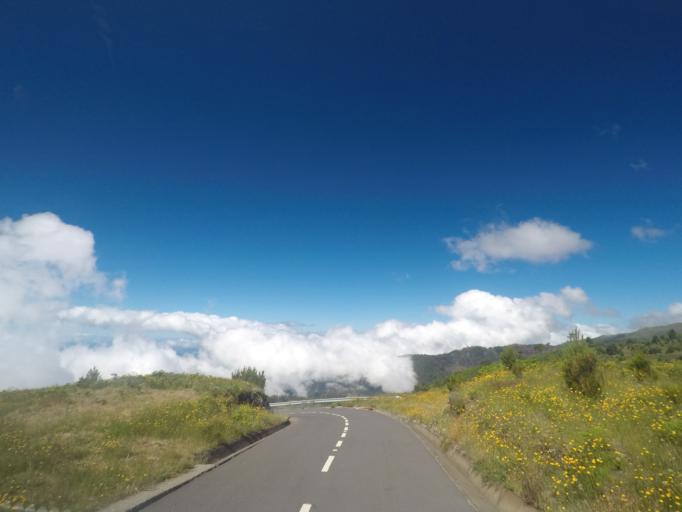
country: PT
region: Madeira
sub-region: Camara de Lobos
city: Curral das Freiras
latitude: 32.7050
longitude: -16.9401
